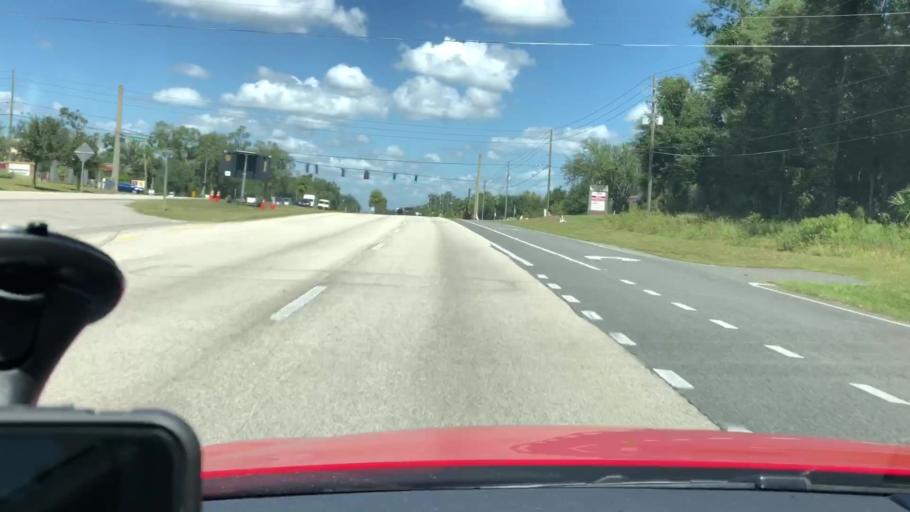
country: US
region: Florida
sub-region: Volusia County
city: Orange City
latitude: 28.9621
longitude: -81.2986
